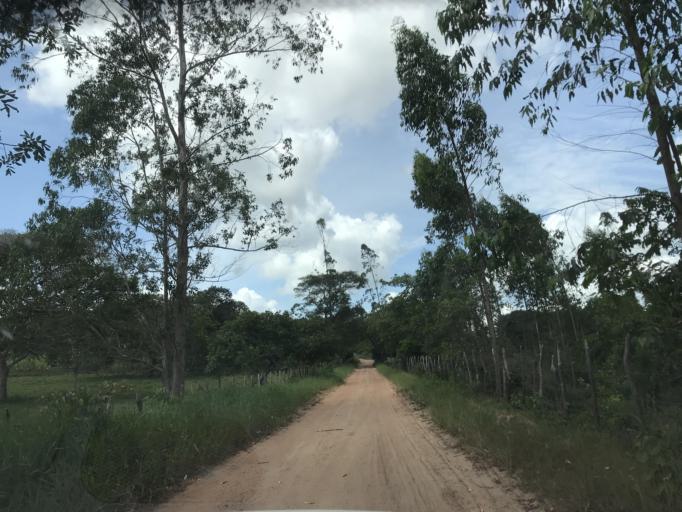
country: BR
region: Bahia
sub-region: Entre Rios
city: Entre Rios
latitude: -12.2386
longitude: -38.0969
